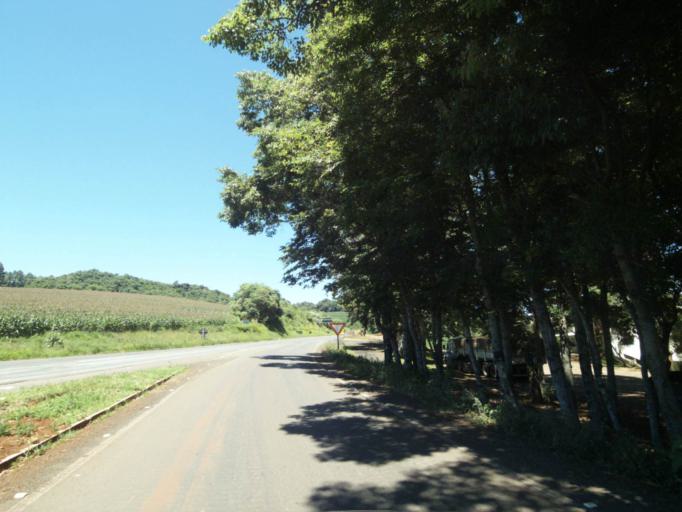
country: BR
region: Santa Catarina
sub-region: Sao Lourenco Do Oeste
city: Sao Lourenco dOeste
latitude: -26.2583
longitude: -52.7881
